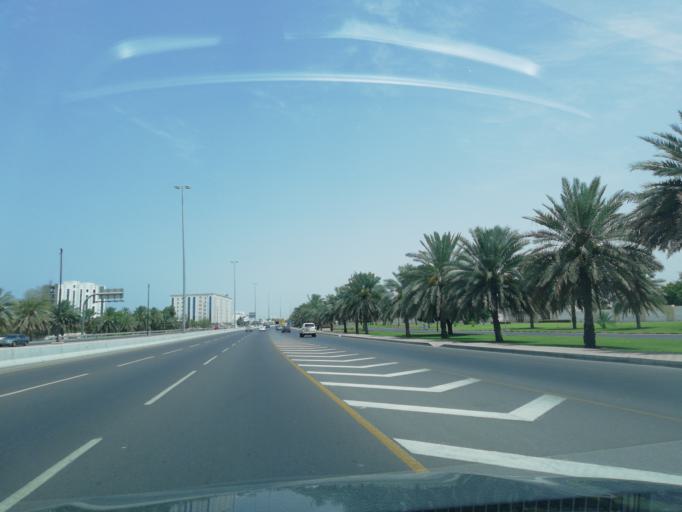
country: OM
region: Muhafazat Masqat
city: As Sib al Jadidah
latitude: 23.6528
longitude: 58.2105
